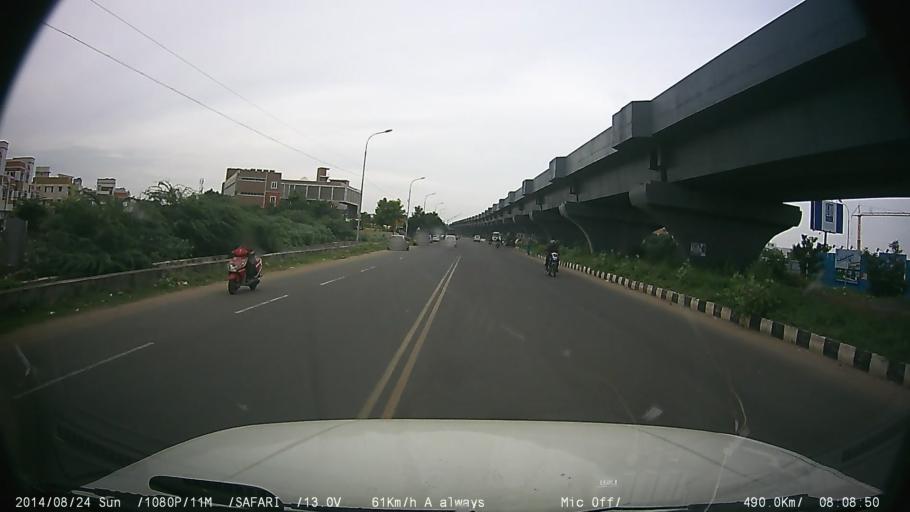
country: IN
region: Tamil Nadu
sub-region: Kancheepuram
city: Madipakkam
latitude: 12.9726
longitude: 80.2110
